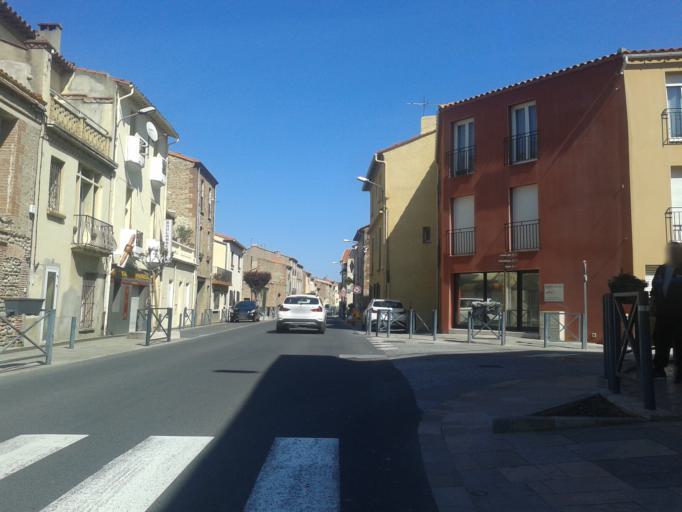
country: FR
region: Languedoc-Roussillon
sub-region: Departement des Pyrenees-Orientales
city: Pezilla-la-Riviere
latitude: 42.6959
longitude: 2.7692
